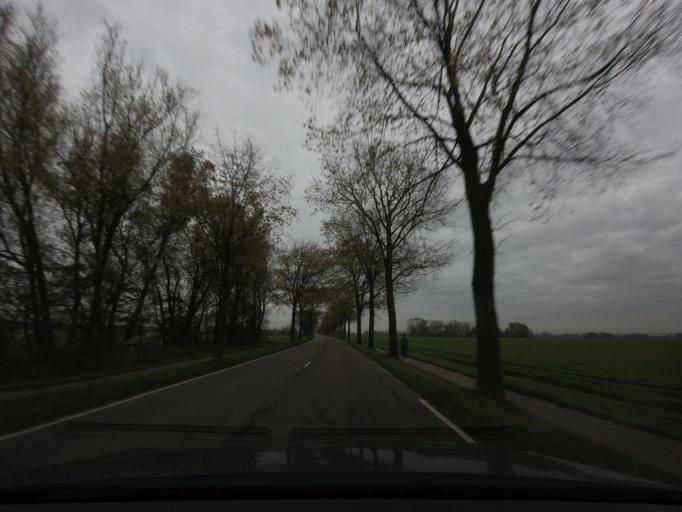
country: NL
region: North Holland
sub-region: Gemeente Alkmaar
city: Alkmaar
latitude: 52.5916
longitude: 4.7340
